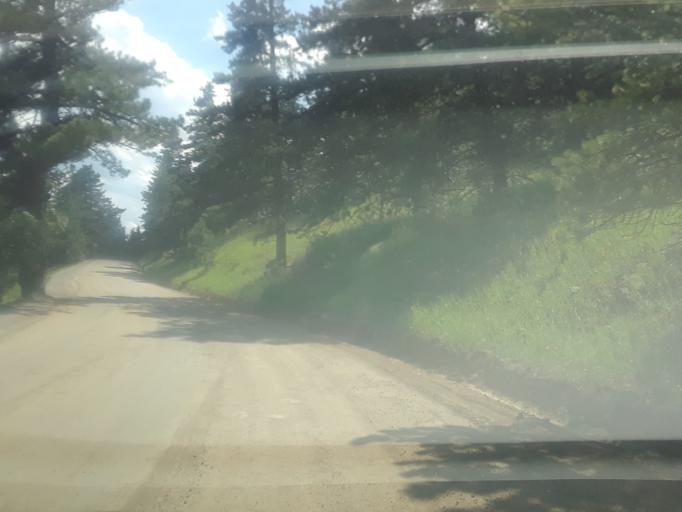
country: US
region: Colorado
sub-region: Boulder County
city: Nederland
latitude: 40.0517
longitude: -105.4613
